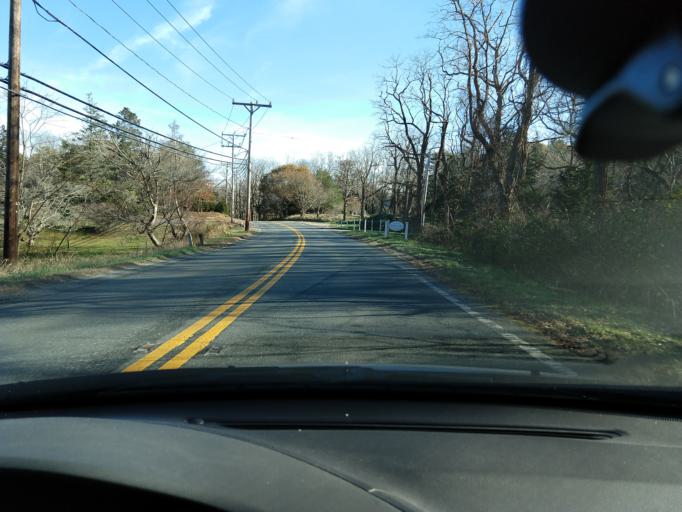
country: US
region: Massachusetts
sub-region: Barnstable County
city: Sandwich
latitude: 41.7491
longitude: -70.4784
